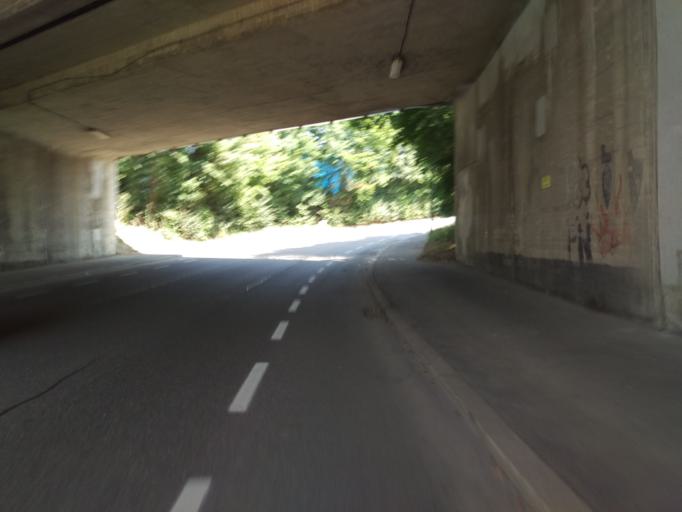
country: AT
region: Styria
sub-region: Politischer Bezirk Graz-Umgebung
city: Feldkirchen bei Graz
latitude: 47.0412
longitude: 15.4671
